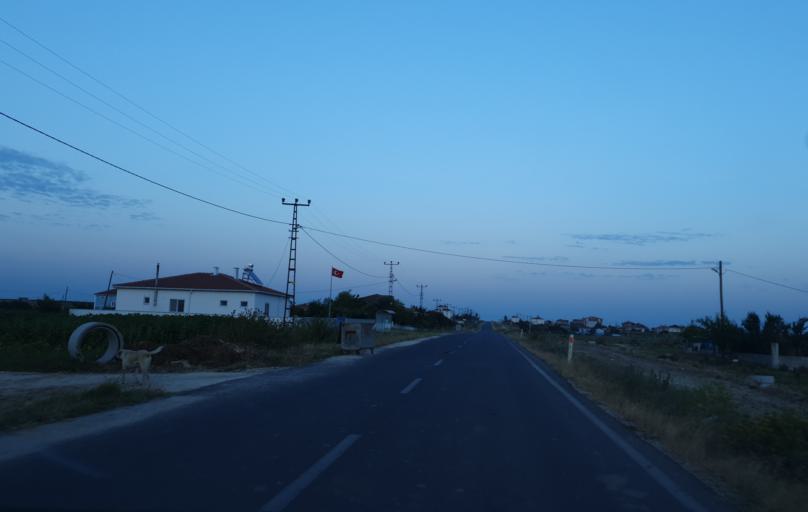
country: TR
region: Tekirdag
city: Velimese
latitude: 41.3462
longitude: 27.8925
